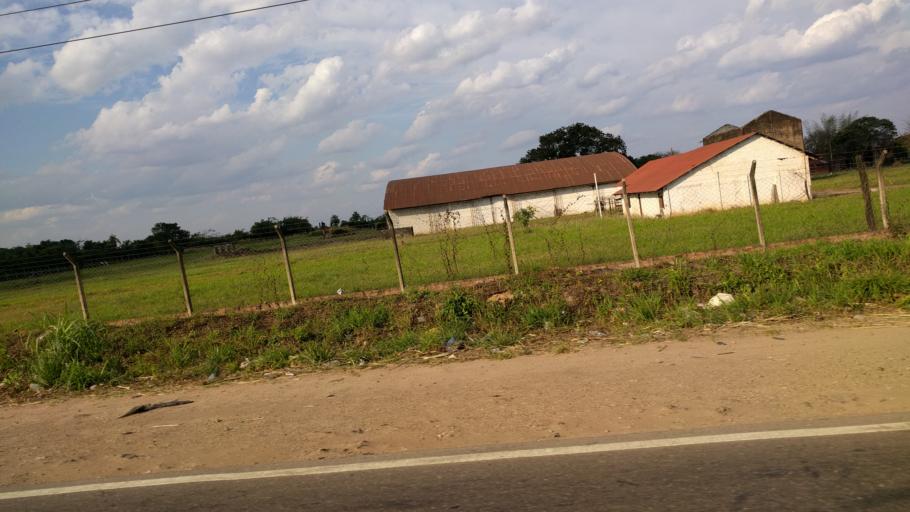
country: BO
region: Santa Cruz
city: Warnes
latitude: -17.5458
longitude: -63.1603
